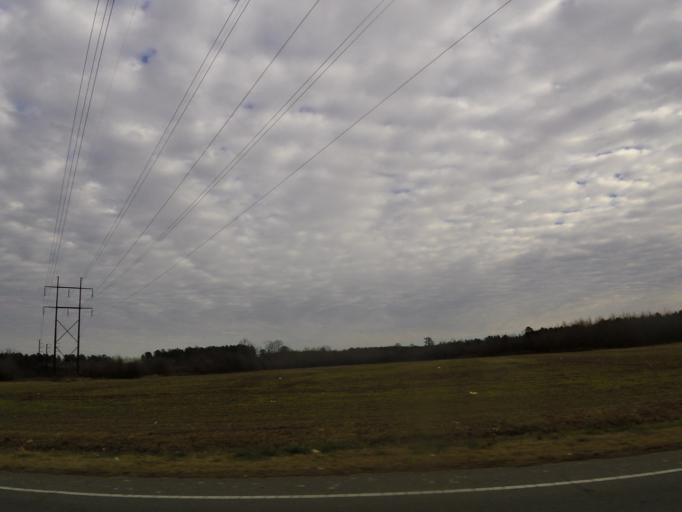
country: US
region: North Carolina
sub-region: Hertford County
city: Murfreesboro
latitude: 36.3389
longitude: -77.2023
